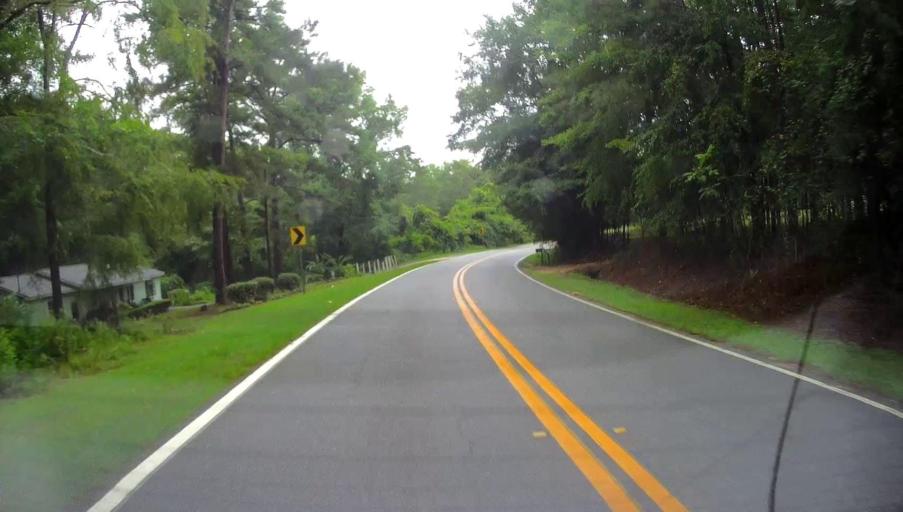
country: US
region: Georgia
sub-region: Bibb County
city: West Point
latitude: 32.7850
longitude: -83.7705
